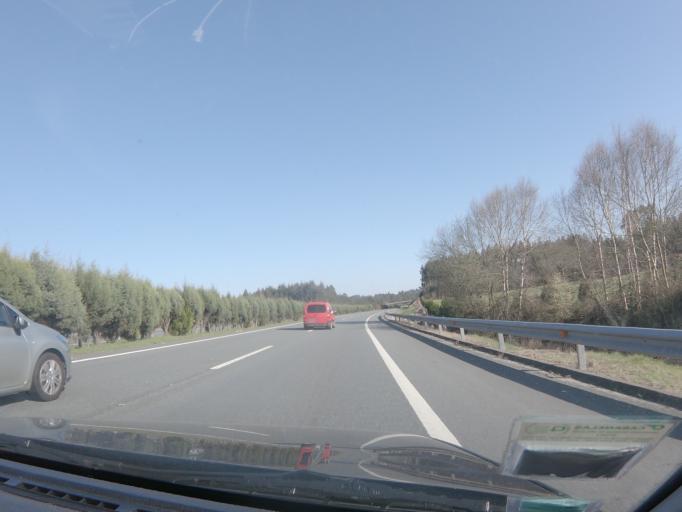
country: ES
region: Galicia
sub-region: Provincia da Coruna
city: Aranga
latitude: 43.1946
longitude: -8.0217
